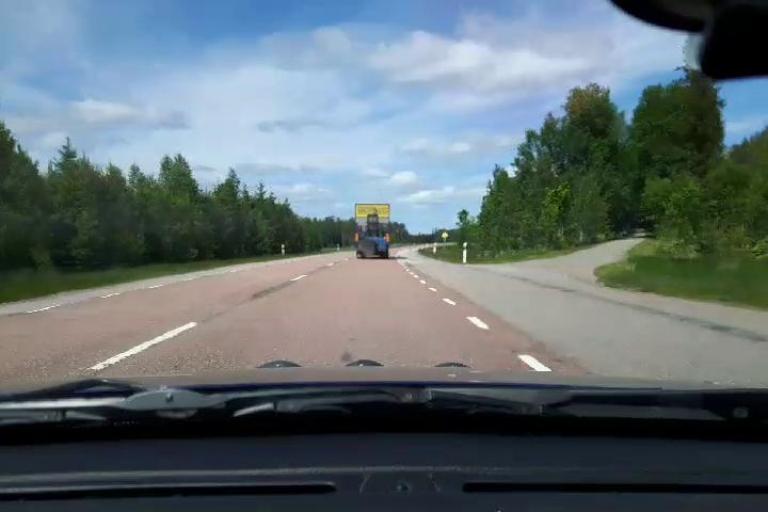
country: SE
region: Uppsala
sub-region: Osthammars Kommun
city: Bjorklinge
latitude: 60.1538
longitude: 17.4916
